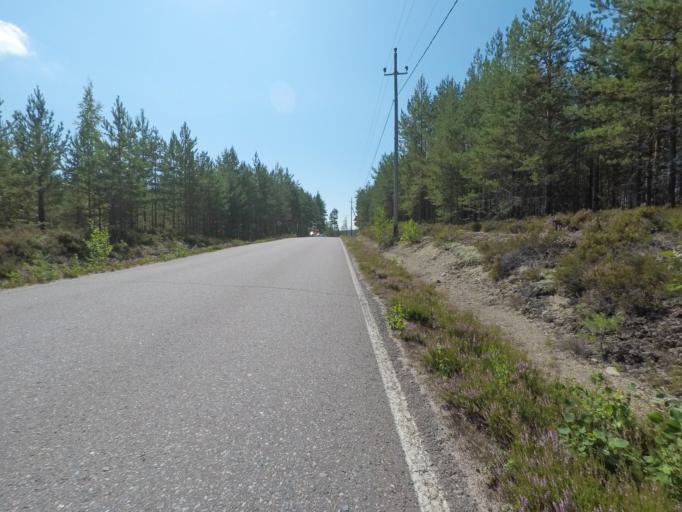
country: FI
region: Southern Savonia
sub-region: Mikkeli
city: Puumala
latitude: 61.4557
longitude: 28.1739
